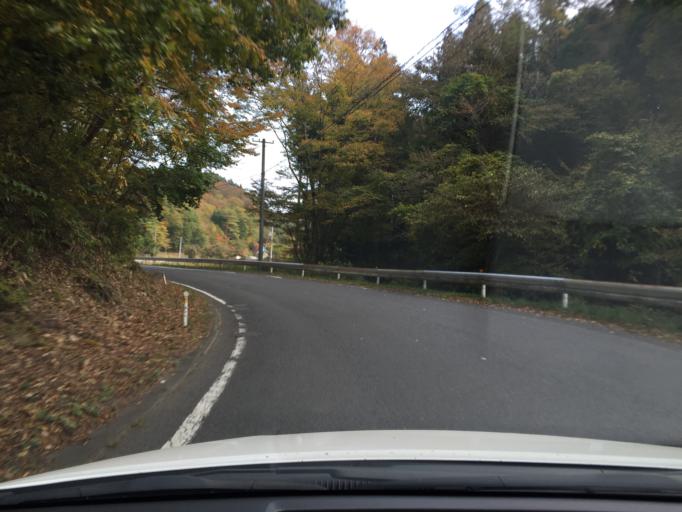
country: JP
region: Fukushima
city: Ishikawa
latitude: 36.9703
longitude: 140.5248
